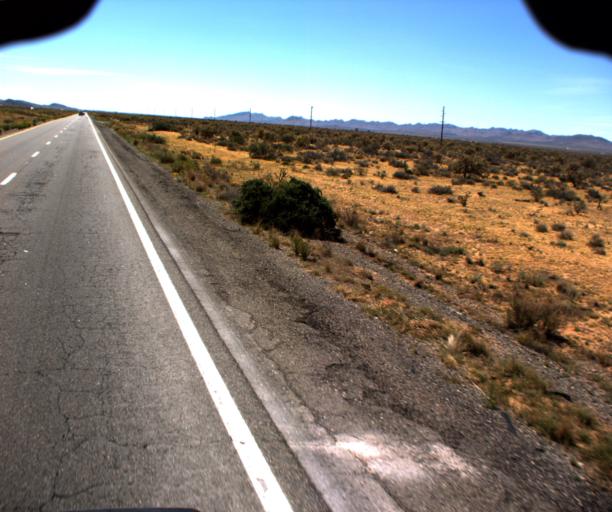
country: US
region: Arizona
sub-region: Mohave County
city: Dolan Springs
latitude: 35.5124
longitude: -114.3408
